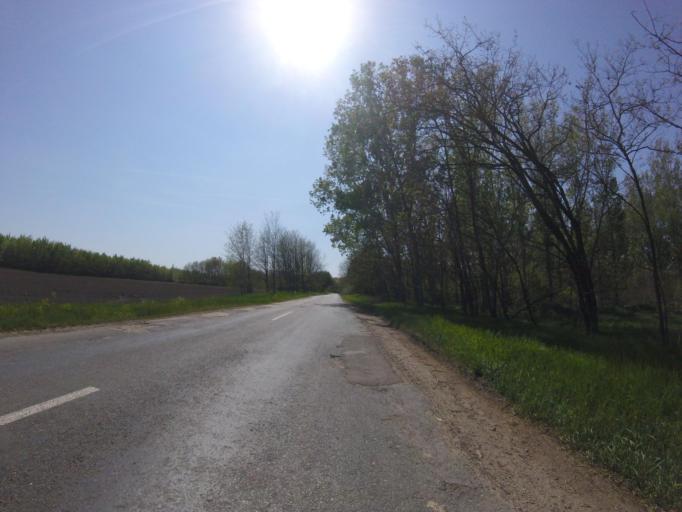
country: HU
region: Pest
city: Ujhartyan
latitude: 47.2308
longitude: 19.4345
